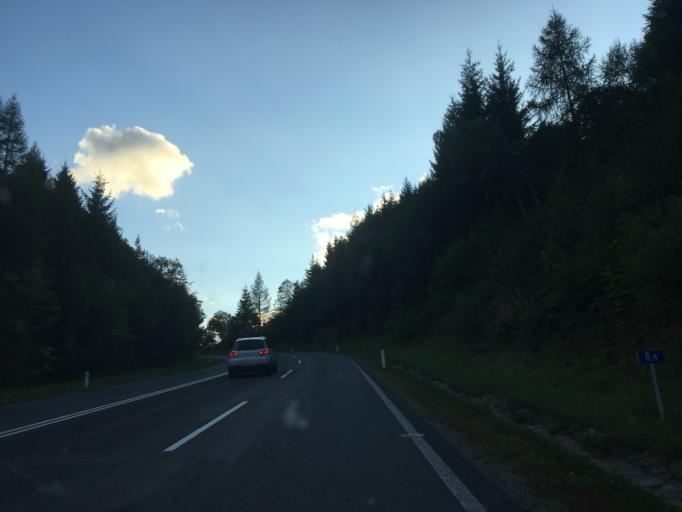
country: AT
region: Styria
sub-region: Politischer Bezirk Murtal
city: Hohentauern
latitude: 47.4346
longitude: 14.4894
